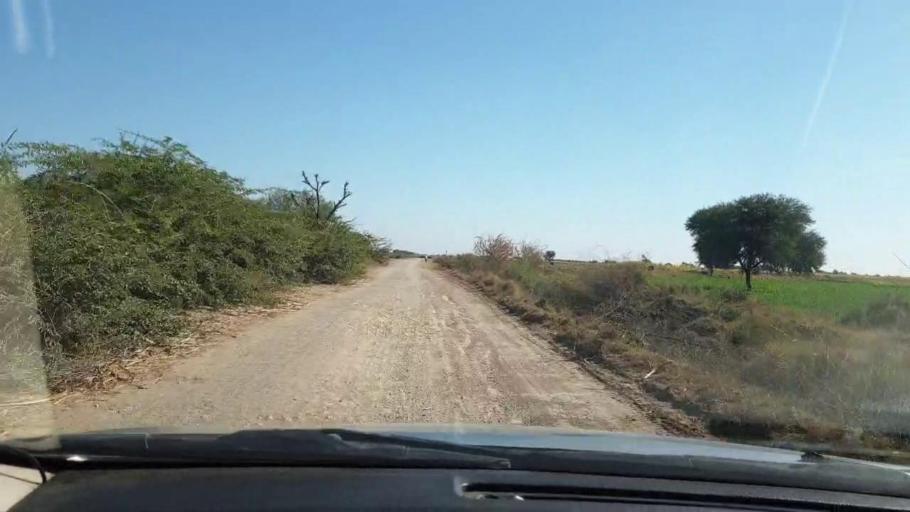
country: PK
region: Sindh
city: Berani
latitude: 25.7218
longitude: 68.9799
